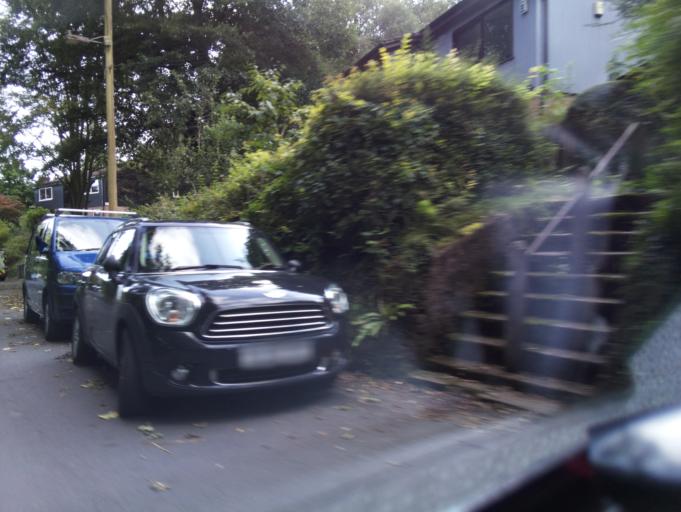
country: GB
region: Wales
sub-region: Cardiff
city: Pentyrch
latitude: 51.5455
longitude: -3.2752
